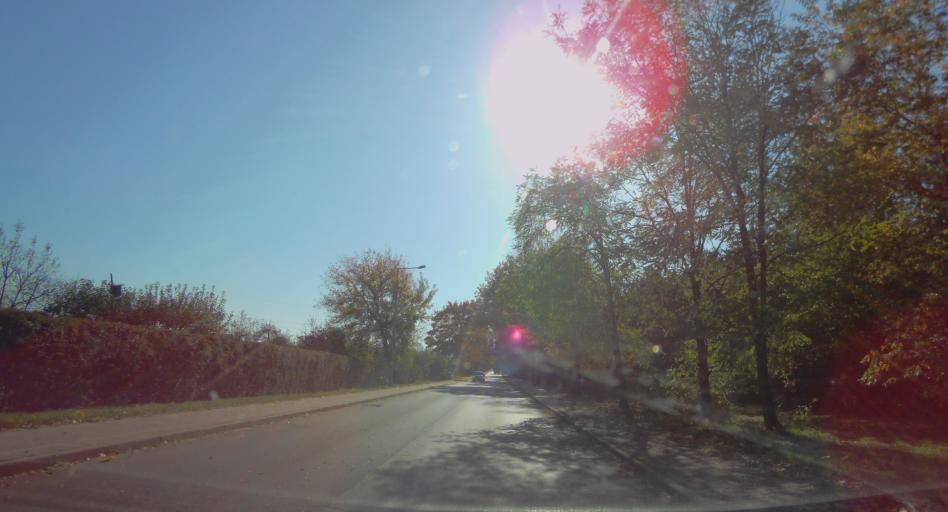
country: PL
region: Subcarpathian Voivodeship
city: Nowa Sarzyna
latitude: 50.3265
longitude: 22.3377
